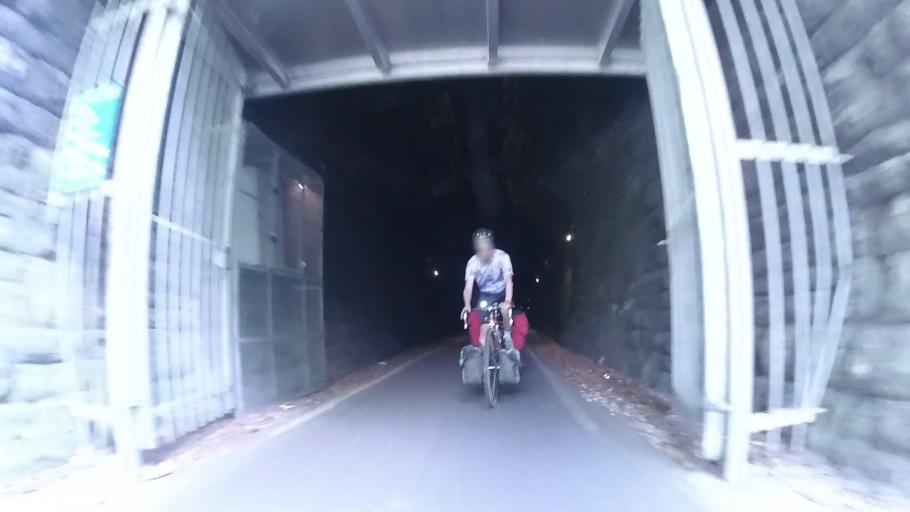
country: GB
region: England
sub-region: Bath and North East Somerset
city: Bath
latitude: 51.3680
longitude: -2.3551
